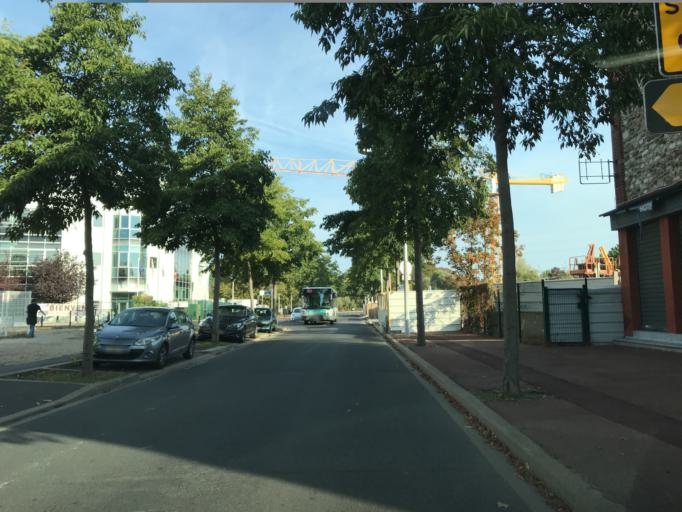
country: FR
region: Ile-de-France
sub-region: Departement des Yvelines
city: Carrieres-sur-Seine
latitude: 48.9029
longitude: 2.1940
